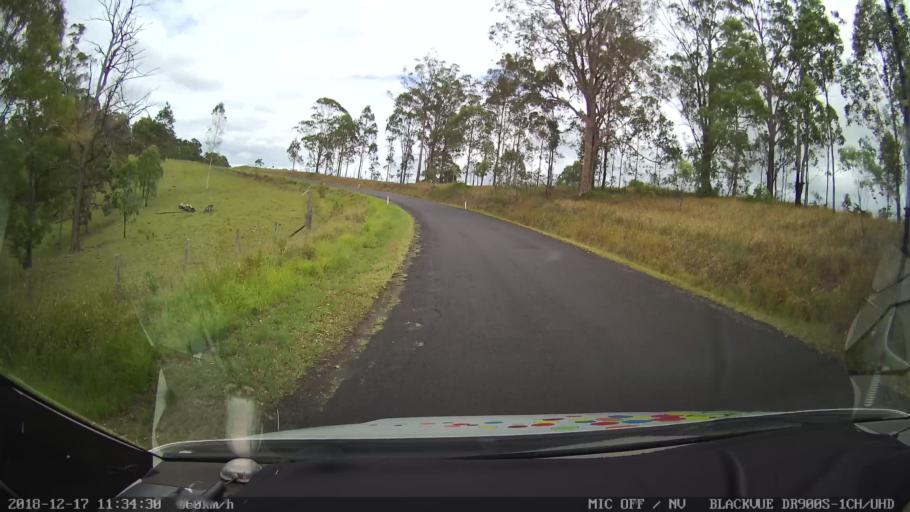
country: AU
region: New South Wales
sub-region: Kyogle
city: Kyogle
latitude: -28.7266
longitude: 152.6130
